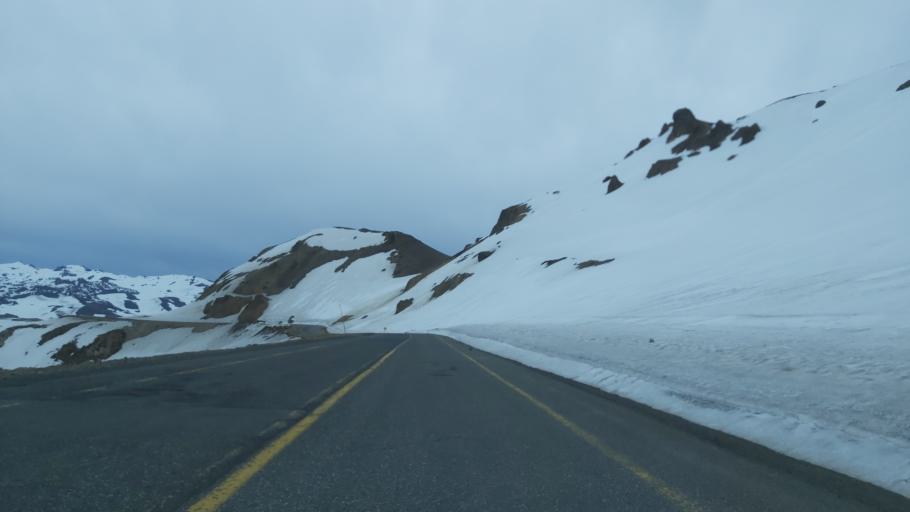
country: CL
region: Maule
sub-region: Provincia de Linares
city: Colbun
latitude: -36.0132
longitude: -70.5103
